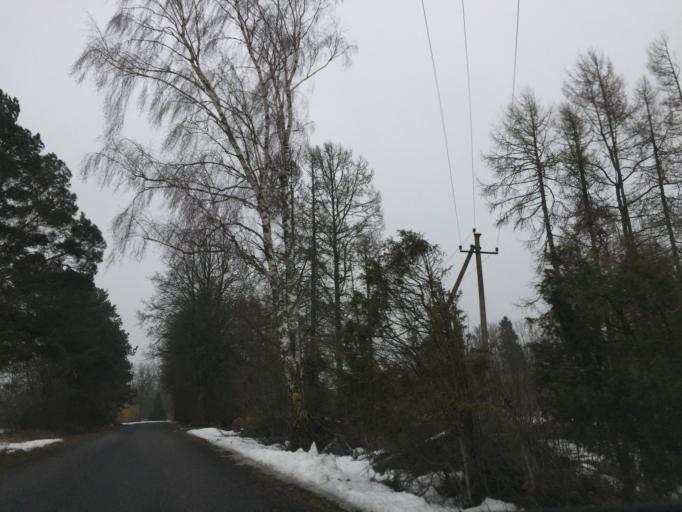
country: EE
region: Saare
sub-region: Kuressaare linn
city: Kuressaare
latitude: 58.2717
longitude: 22.5805
